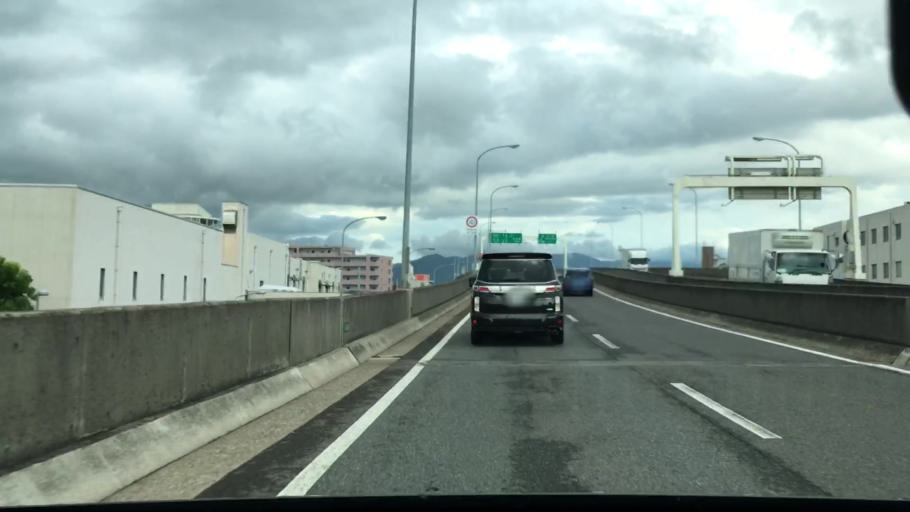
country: JP
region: Fukuoka
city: Fukuoka-shi
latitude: 33.6327
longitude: 130.4316
